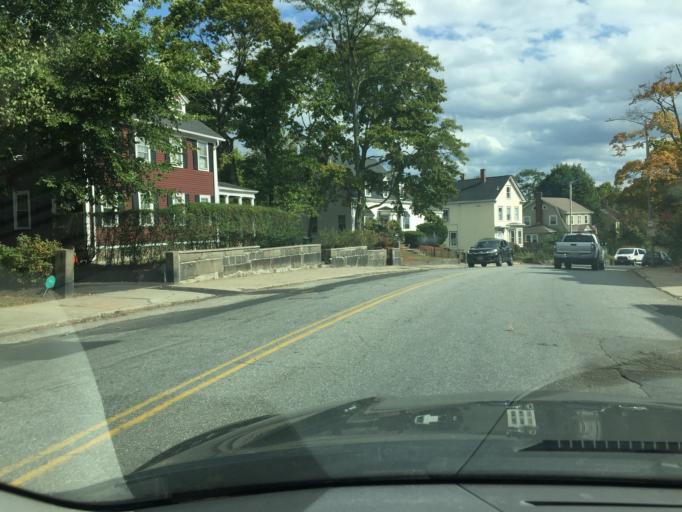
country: US
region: Massachusetts
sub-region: Middlesex County
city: Medford
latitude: 42.4218
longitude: -71.1227
